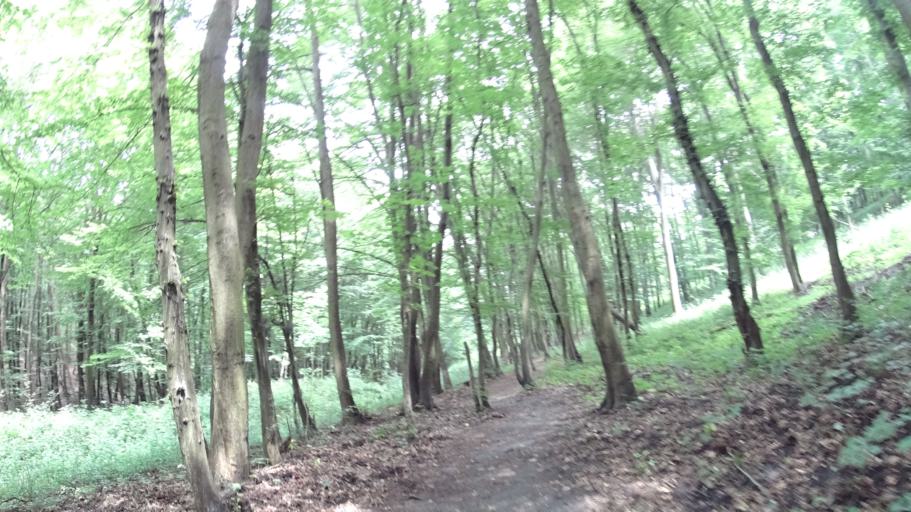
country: HU
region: Pest
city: Nagymaros
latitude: 47.7996
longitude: 18.9250
